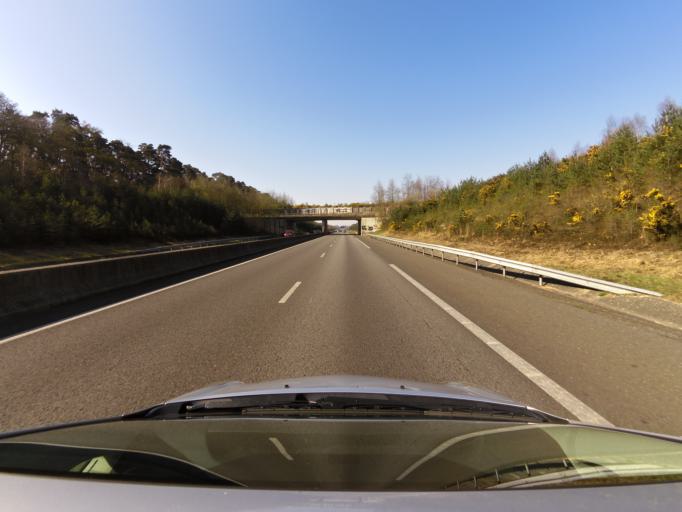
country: FR
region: Brittany
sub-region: Departement d'Ille-et-Vilaine
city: Fouillard
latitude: 48.1873
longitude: -1.5488
